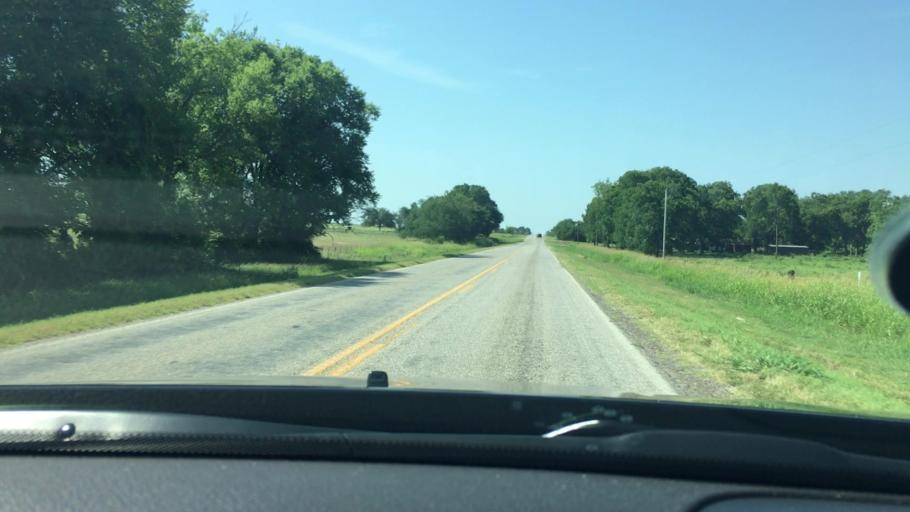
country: US
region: Oklahoma
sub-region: Johnston County
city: Tishomingo
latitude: 34.2913
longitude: -96.4248
